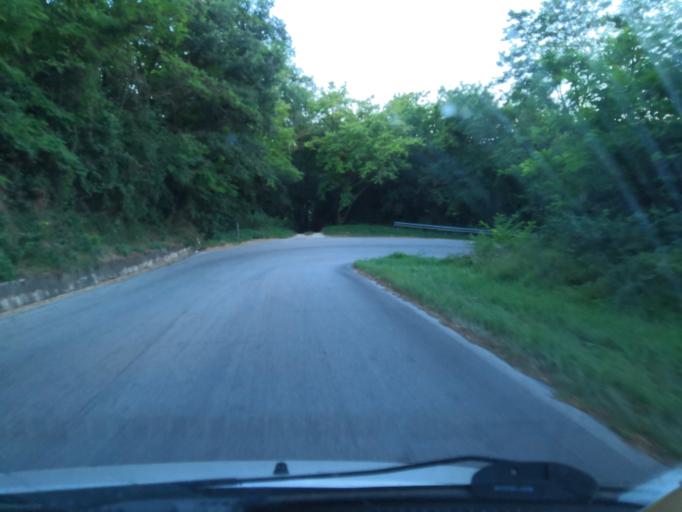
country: IT
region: Molise
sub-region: Provincia di Campobasso
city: Jelsi
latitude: 41.5131
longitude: 14.7928
